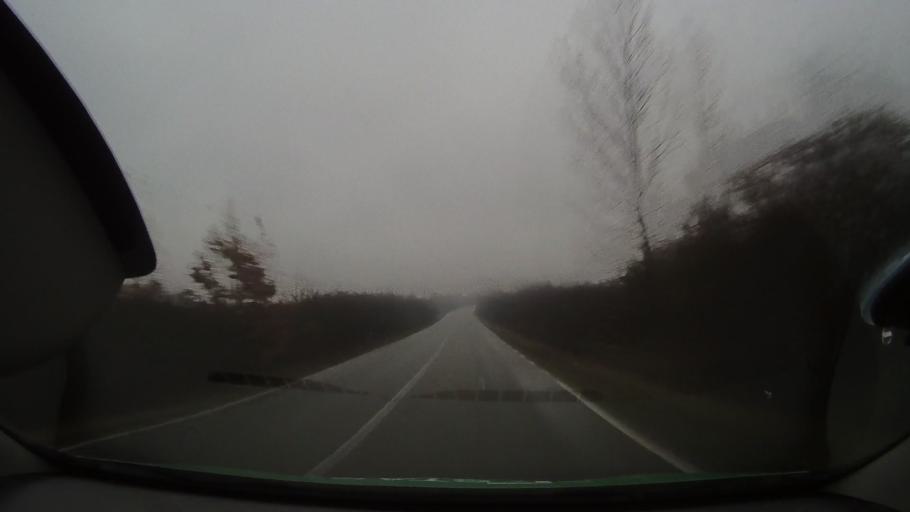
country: RO
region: Arad
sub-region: Comuna Craiova
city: Craiova
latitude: 46.6010
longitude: 21.9664
